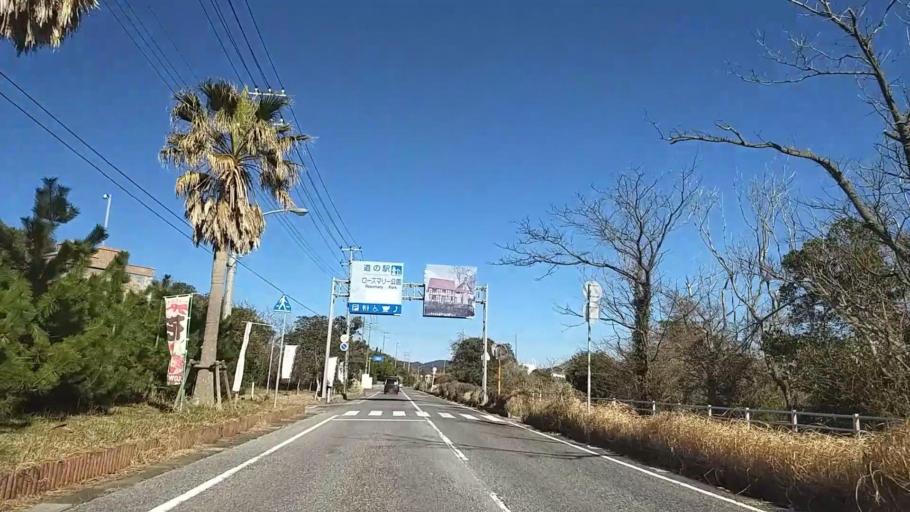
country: JP
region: Chiba
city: Tateyama
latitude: 35.0080
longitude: 139.9768
